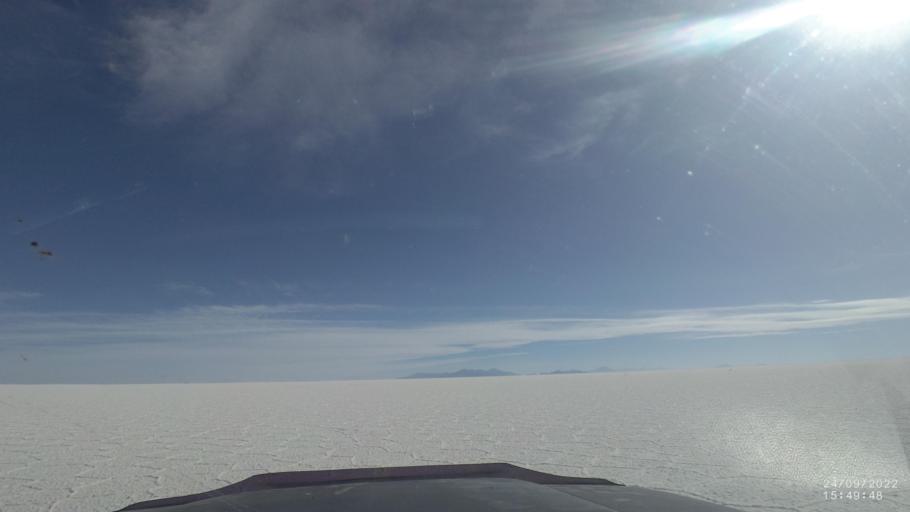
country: BO
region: Potosi
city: Colchani
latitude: -20.3037
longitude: -67.2444
